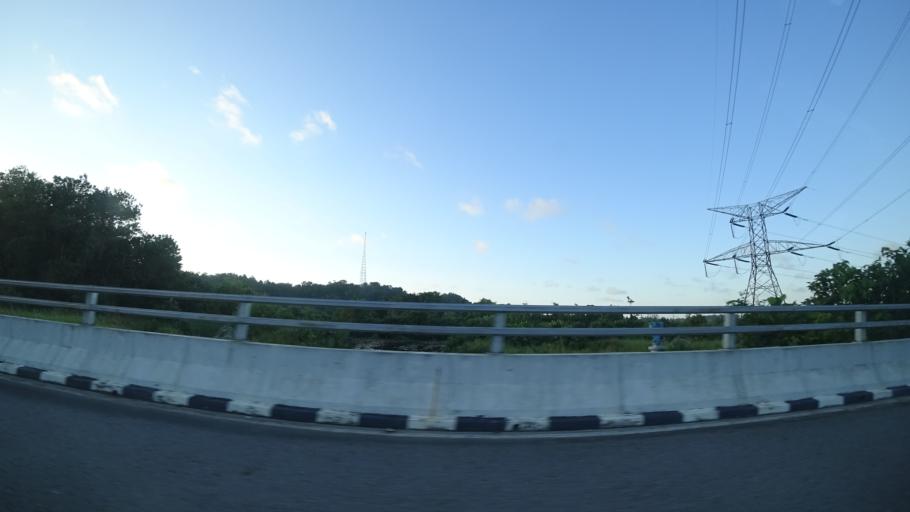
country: BN
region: Tutong
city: Tutong
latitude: 4.8231
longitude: 114.6806
